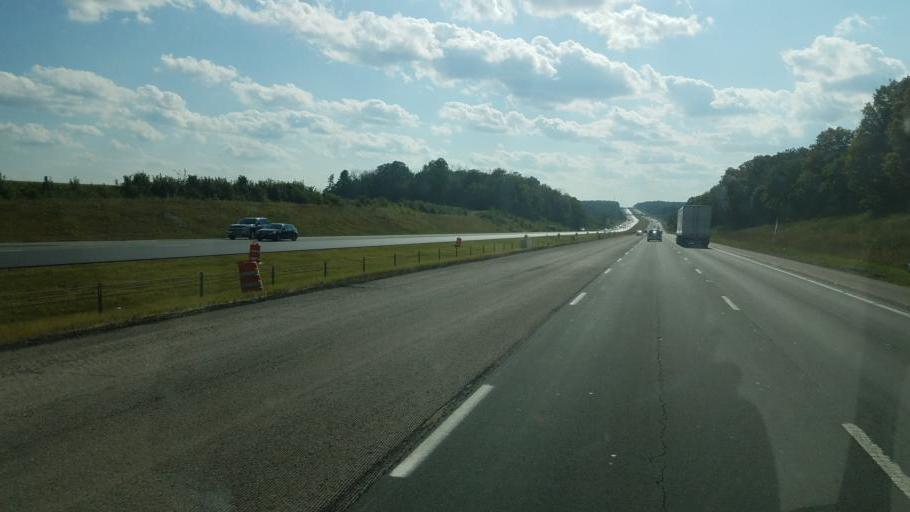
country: US
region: Ohio
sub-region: Ashland County
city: Ashland
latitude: 40.8348
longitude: -82.3035
